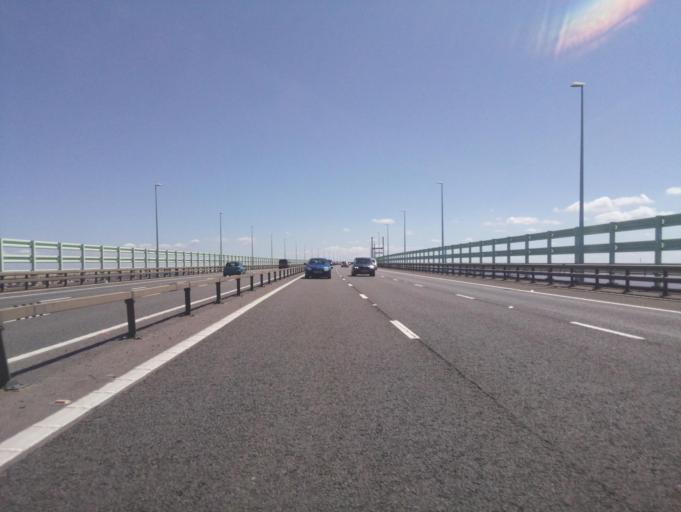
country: GB
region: Wales
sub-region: Monmouthshire
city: Caldicot
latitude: 51.5818
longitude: -2.7290
